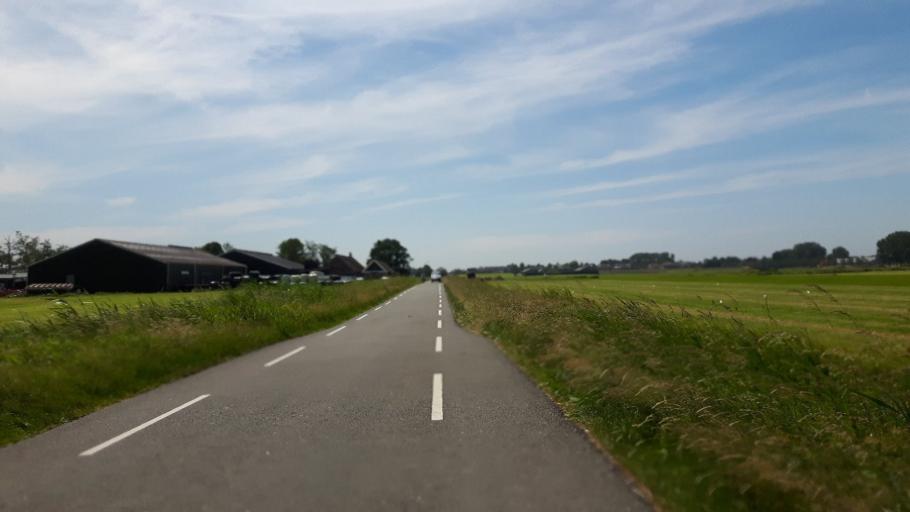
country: NL
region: South Holland
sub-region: Gemeente Nieuwkoop
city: Nieuwkoop
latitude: 52.1416
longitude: 4.7443
